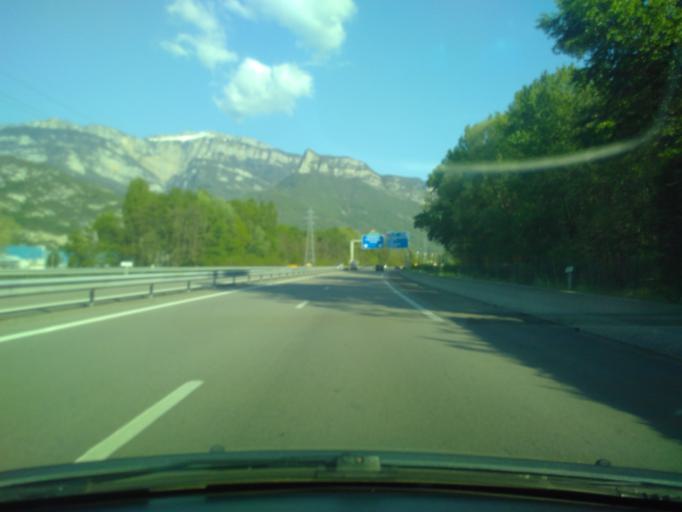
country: FR
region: Rhone-Alpes
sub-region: Departement de l'Isere
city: Voreppe
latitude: 45.3043
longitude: 5.6074
